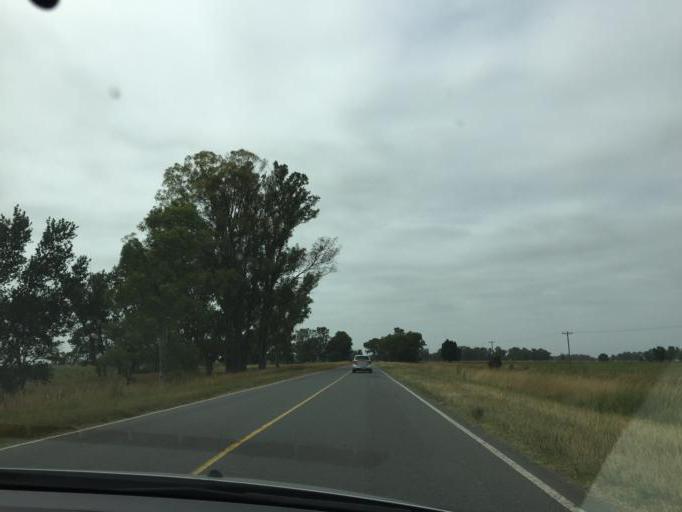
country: AR
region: Buenos Aires
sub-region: Partido de Las Flores
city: Las Flores
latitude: -36.1934
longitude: -59.0552
